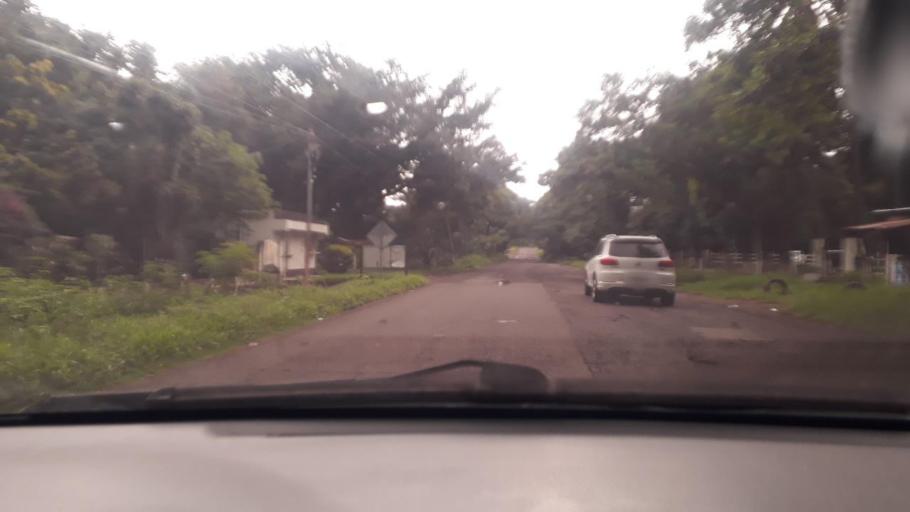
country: GT
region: Jutiapa
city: Jalpatagua
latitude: 14.1240
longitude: -89.9856
